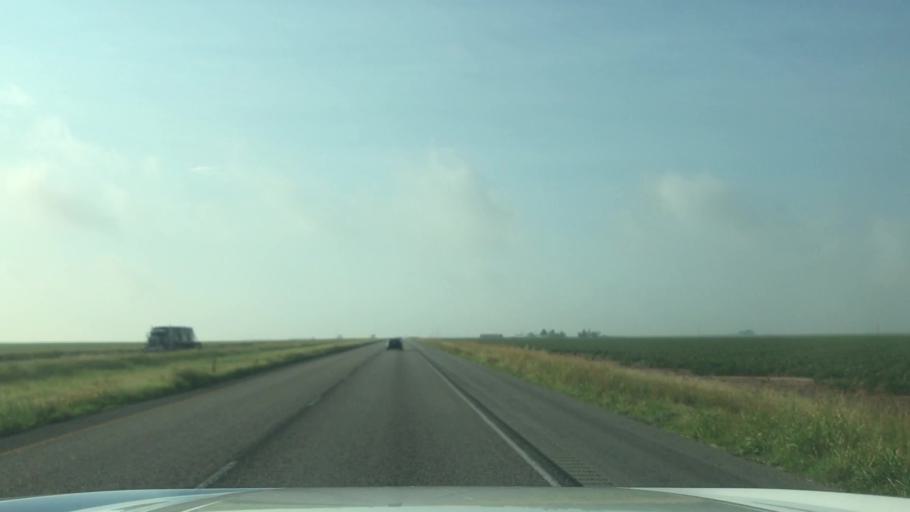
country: US
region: Texas
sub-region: Lubbock County
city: Slaton
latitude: 33.3234
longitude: -101.5283
